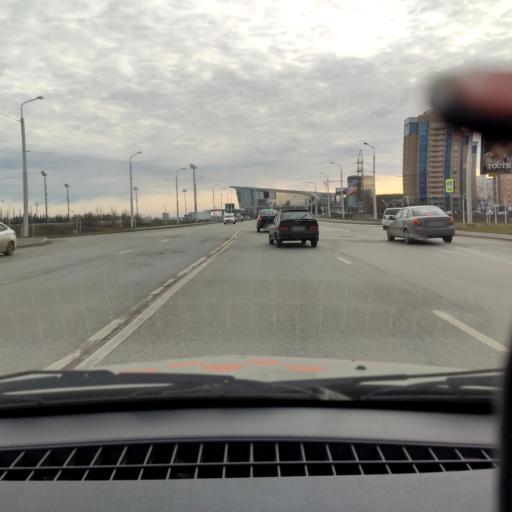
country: RU
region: Bashkortostan
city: Ufa
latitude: 54.7562
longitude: 56.0316
